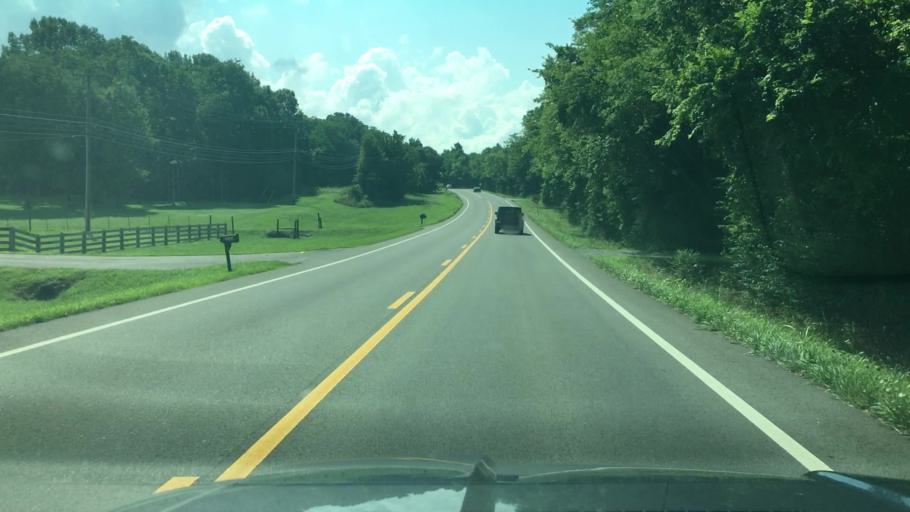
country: US
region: Tennessee
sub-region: Williamson County
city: Nolensville
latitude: 35.8735
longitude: -86.7318
